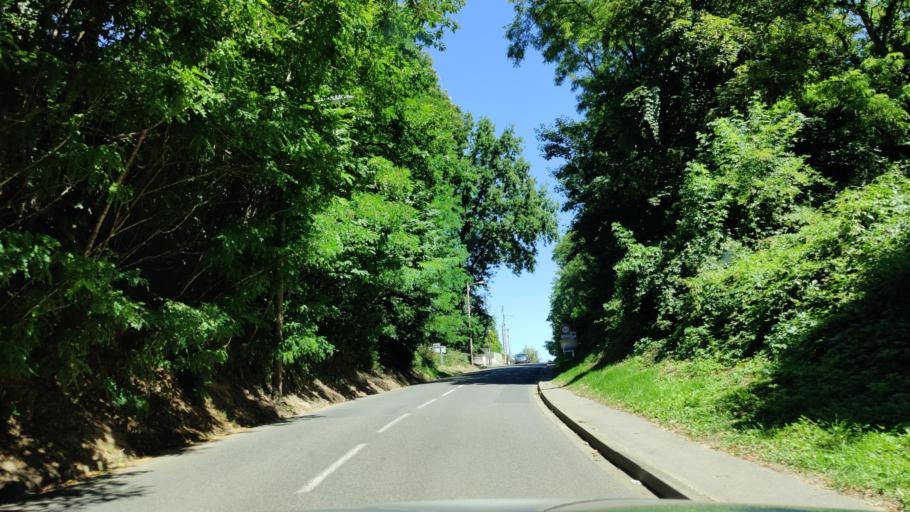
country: FR
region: Ile-de-France
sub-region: Departement de l'Essonne
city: Bruyeres-le-Chatel
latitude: 48.5954
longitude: 2.1810
